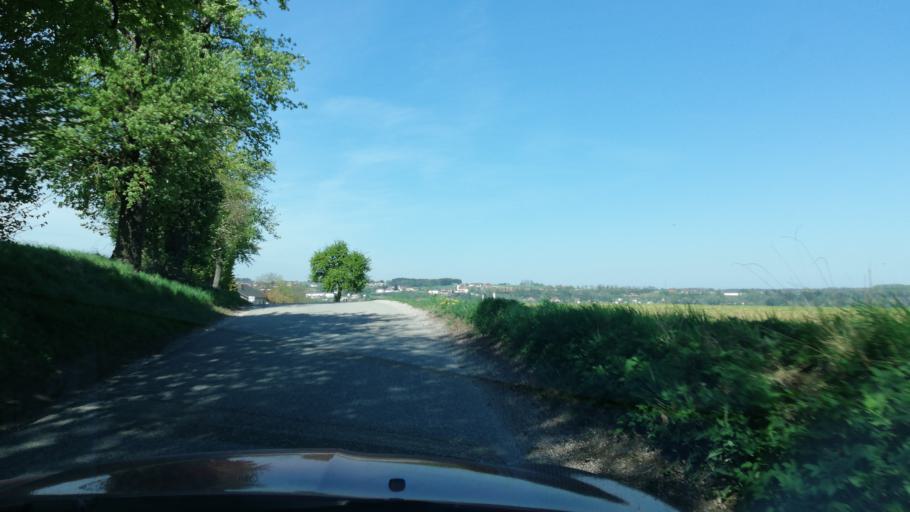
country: AT
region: Upper Austria
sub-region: Politischer Bezirk Kirchdorf an der Krems
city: Kremsmunster
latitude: 48.0484
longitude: 14.1554
